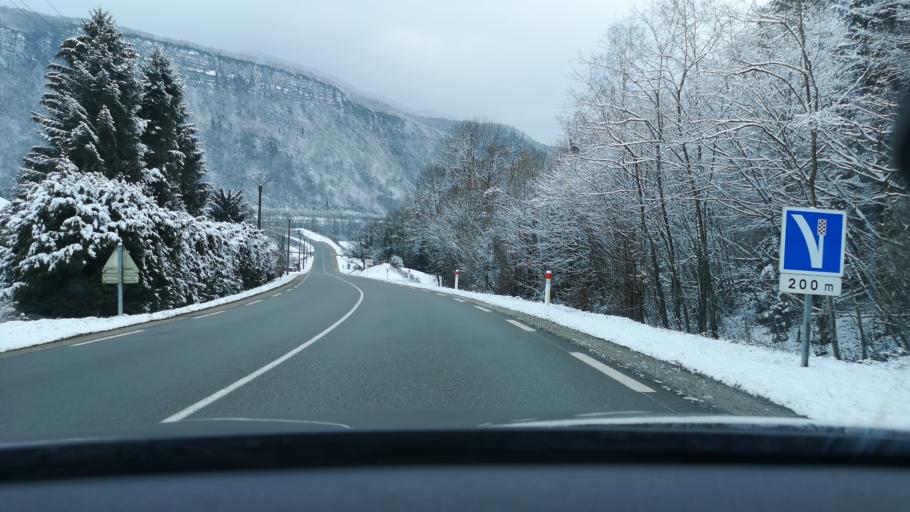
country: FR
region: Rhone-Alpes
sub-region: Departement de l'Ain
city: Dortan
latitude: 46.3692
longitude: 5.7040
